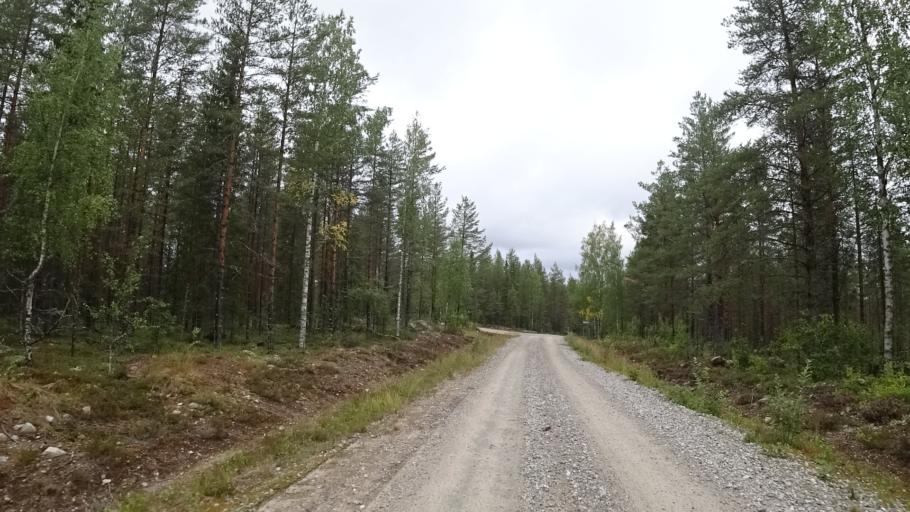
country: FI
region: North Karelia
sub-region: Pielisen Karjala
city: Lieksa
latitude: 63.4771
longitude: 30.2592
